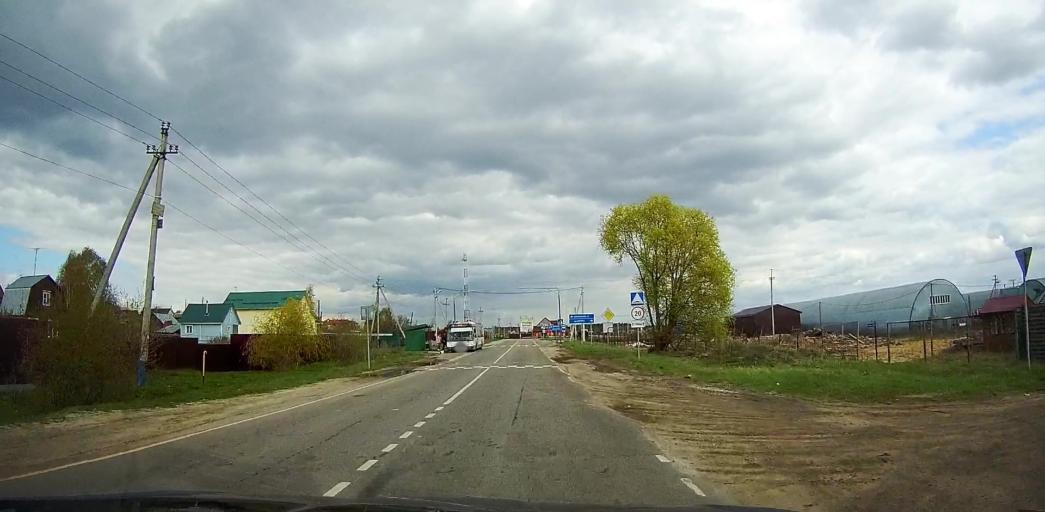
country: RU
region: Moskovskaya
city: Imeni Tsyurupy
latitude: 55.4961
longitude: 38.6220
